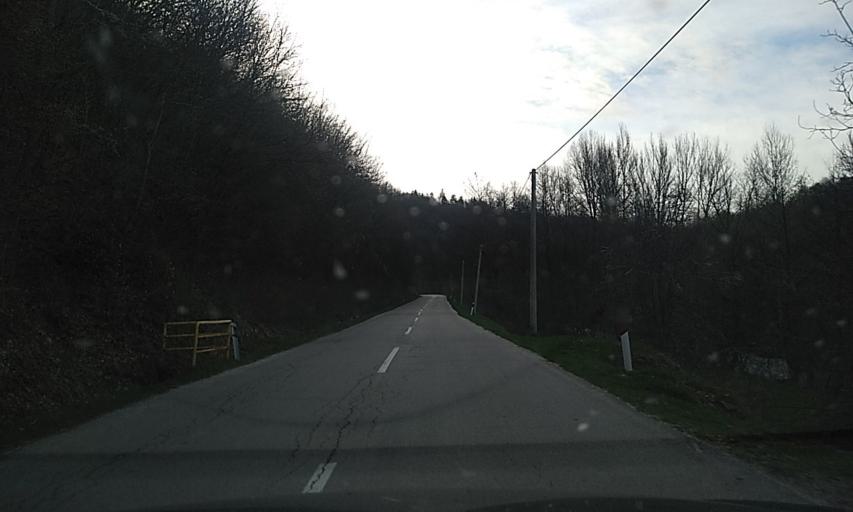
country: RS
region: Central Serbia
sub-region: Pcinjski Okrug
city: Bosilegrad
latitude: 42.4299
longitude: 22.5165
